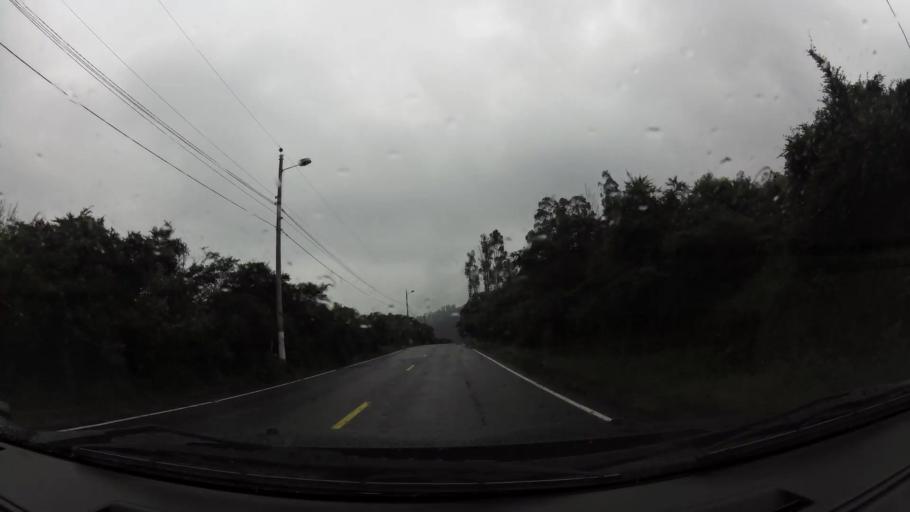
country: EC
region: Pichincha
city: Sangolqui
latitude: -0.2766
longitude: -78.4482
